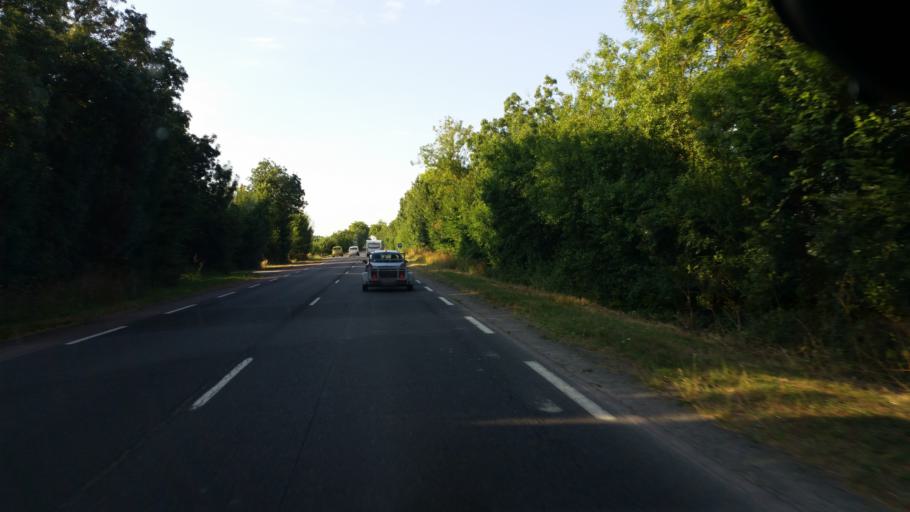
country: FR
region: Poitou-Charentes
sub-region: Departement de la Charente-Maritime
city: Marans
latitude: 46.3289
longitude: -0.9954
